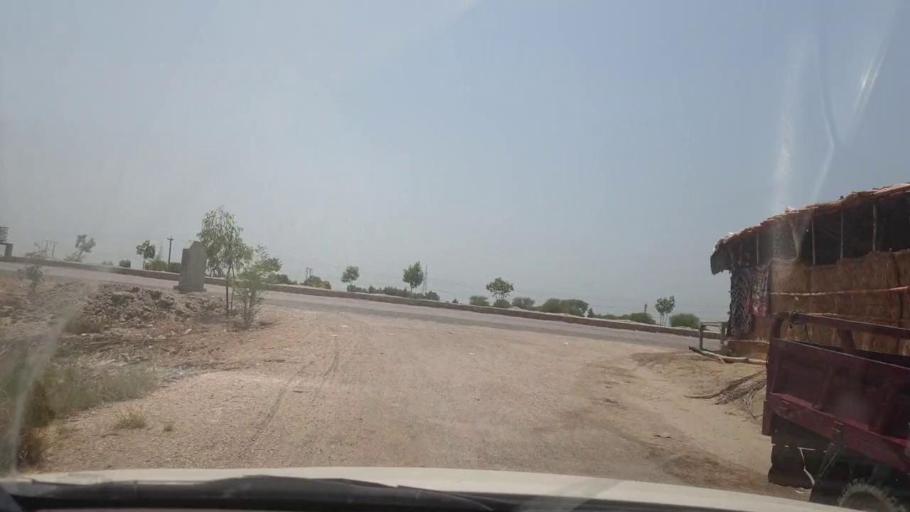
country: PK
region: Sindh
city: Lakhi
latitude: 27.8715
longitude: 68.6886
